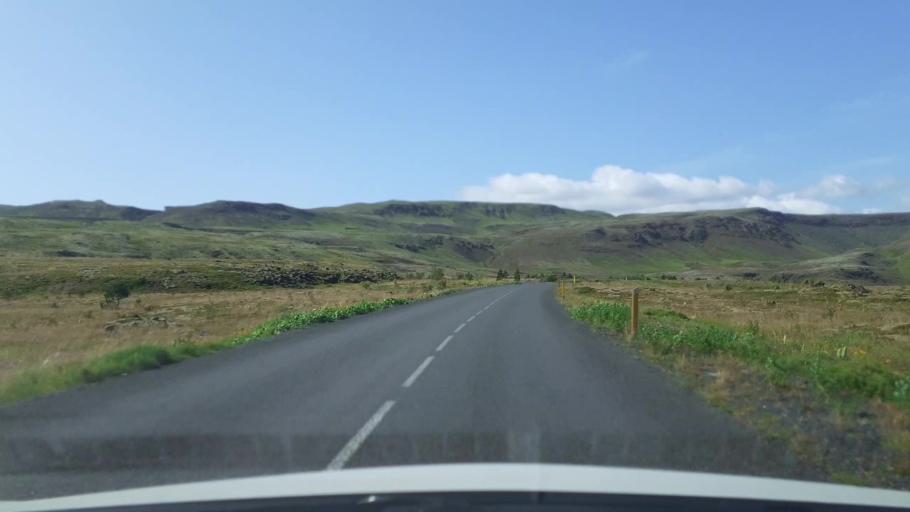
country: IS
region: South
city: Hveragerdi
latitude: 64.0139
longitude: -21.2069
